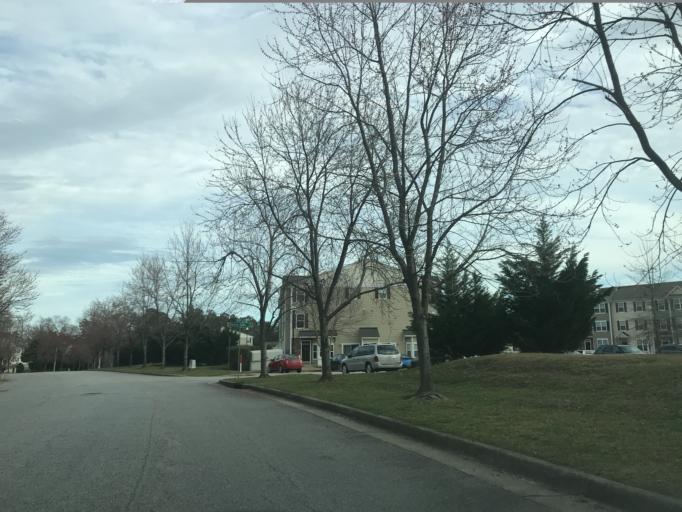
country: US
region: North Carolina
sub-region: Wake County
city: Wake Forest
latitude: 35.9233
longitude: -78.5691
